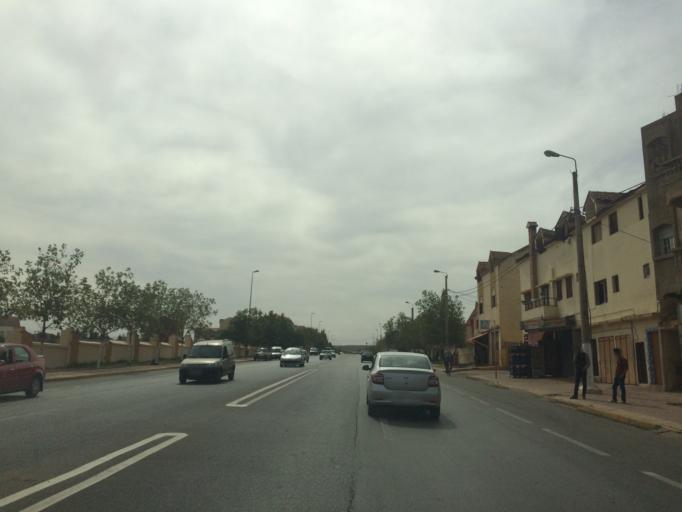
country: MA
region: Meknes-Tafilalet
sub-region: El-Hajeb
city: El Hajeb
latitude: 33.6784
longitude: -5.3727
